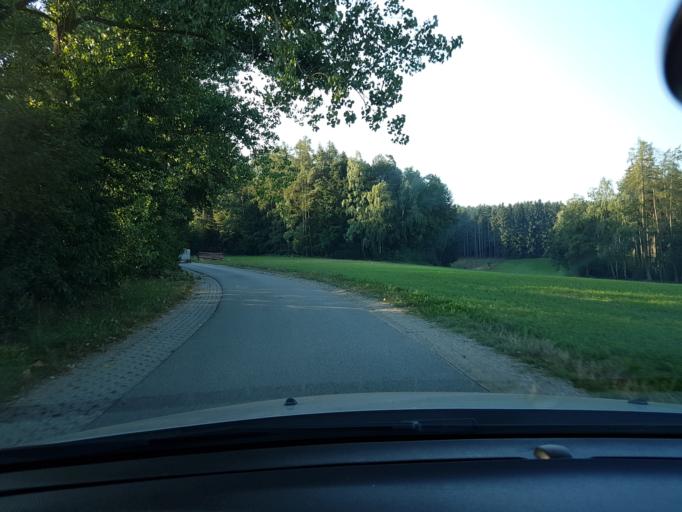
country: DE
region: Bavaria
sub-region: Upper Bavaria
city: Egglkofen
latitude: 48.4349
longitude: 12.4768
